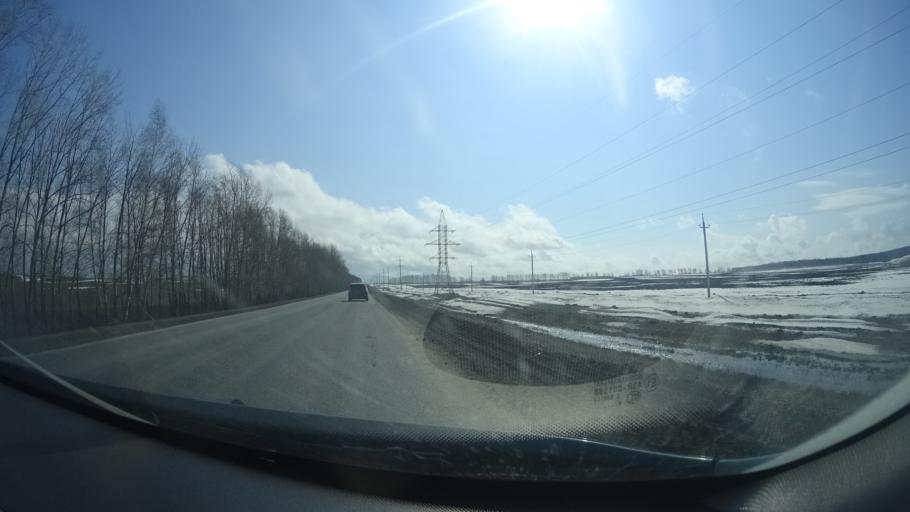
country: RU
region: Bashkortostan
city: Mikhaylovka
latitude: 54.8621
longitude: 55.7539
